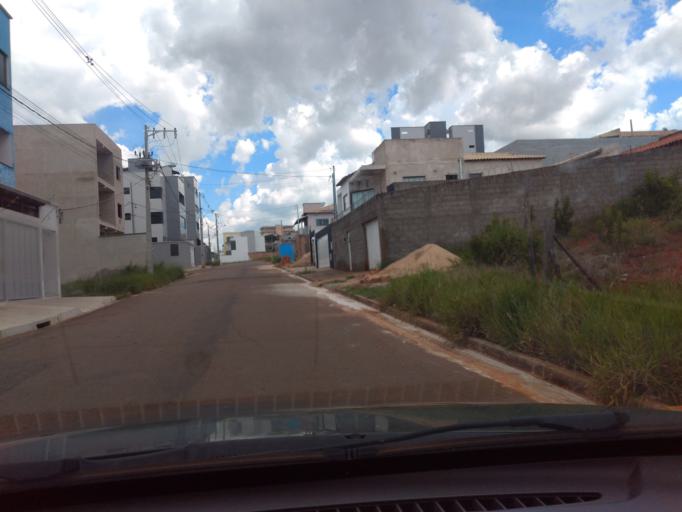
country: BR
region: Minas Gerais
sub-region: Tres Coracoes
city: Tres Coracoes
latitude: -21.6823
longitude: -45.2639
